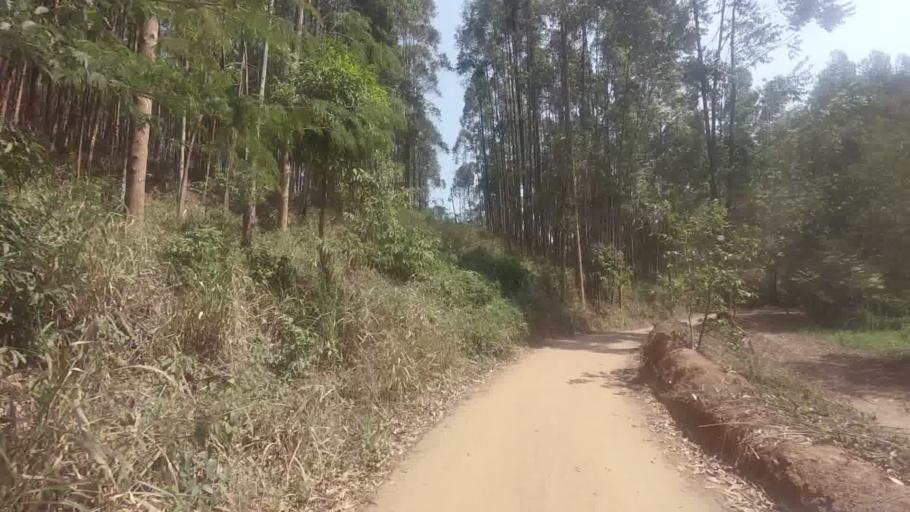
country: BR
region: Espirito Santo
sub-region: Sao Jose Do Calcado
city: Sao Jose do Calcado
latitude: -20.9997
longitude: -41.5043
